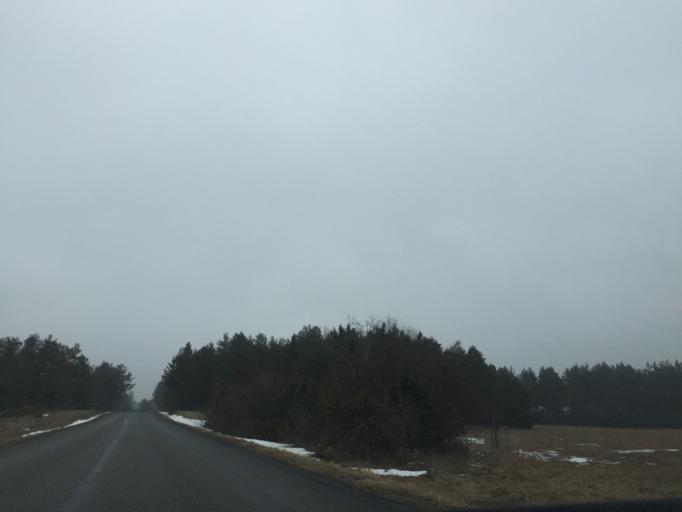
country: EE
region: Saare
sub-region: Orissaare vald
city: Orissaare
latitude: 58.4124
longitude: 22.8140
